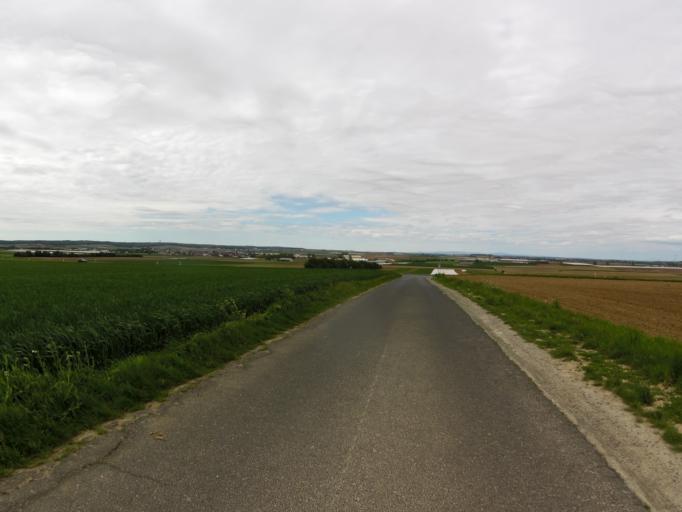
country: DE
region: Bavaria
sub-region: Regierungsbezirk Unterfranken
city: Oberpleichfeld
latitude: 49.8507
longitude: 10.0713
